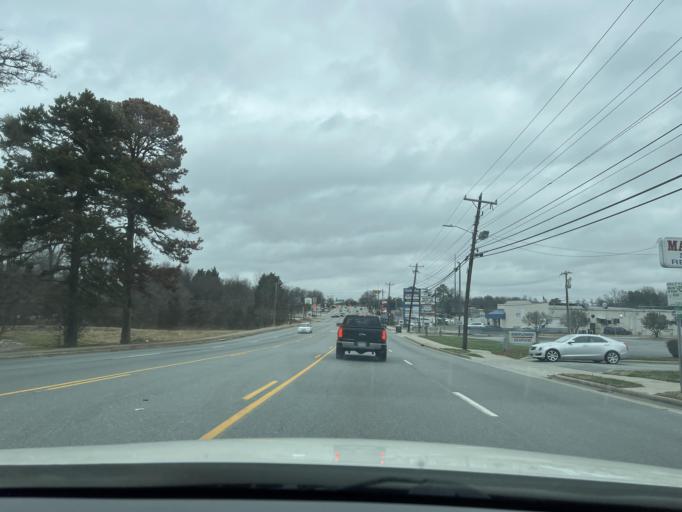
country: US
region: North Carolina
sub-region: Guilford County
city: Greensboro
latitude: 36.0280
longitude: -79.8021
